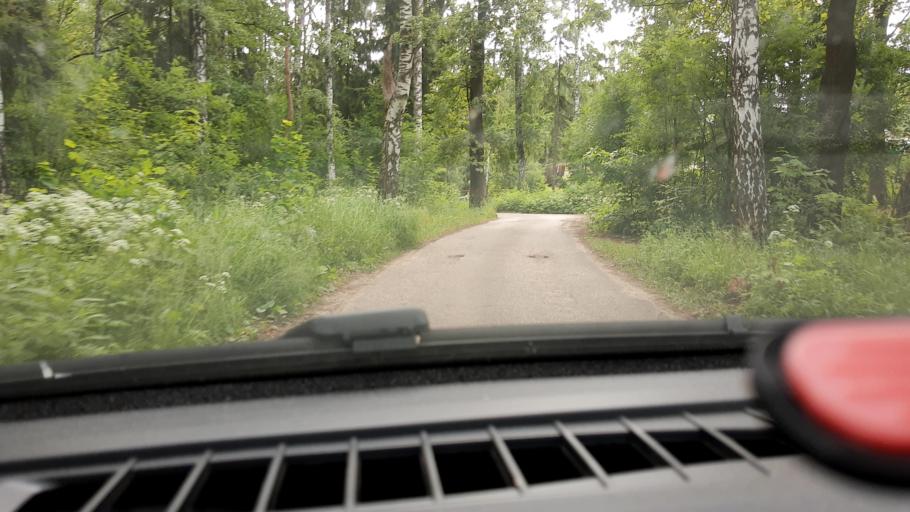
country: RU
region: Nizjnij Novgorod
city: Afonino
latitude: 56.1862
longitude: 44.1053
